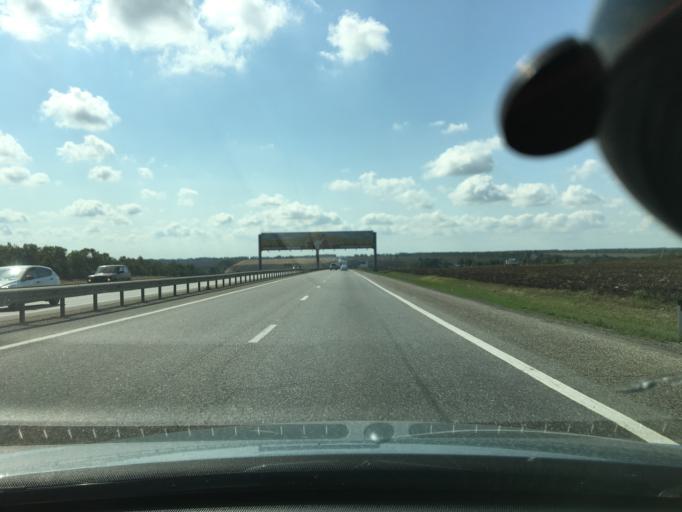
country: RU
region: Krasnodarskiy
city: Krasnoye
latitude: 46.7783
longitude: 39.6643
